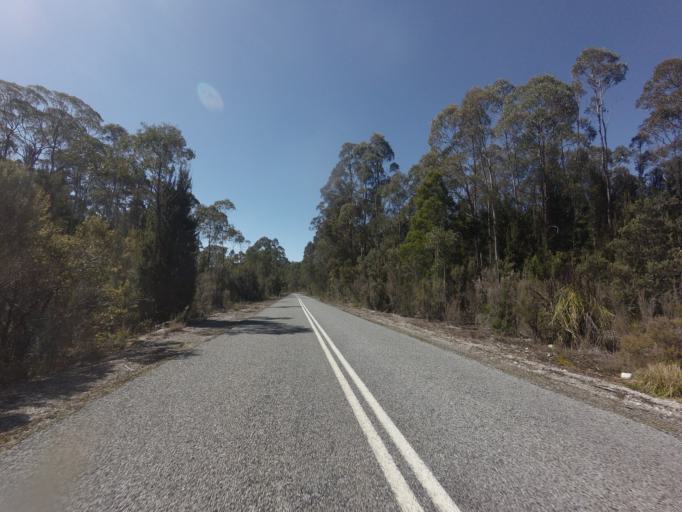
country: AU
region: Tasmania
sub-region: Huon Valley
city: Geeveston
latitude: -42.7693
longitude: 146.3969
